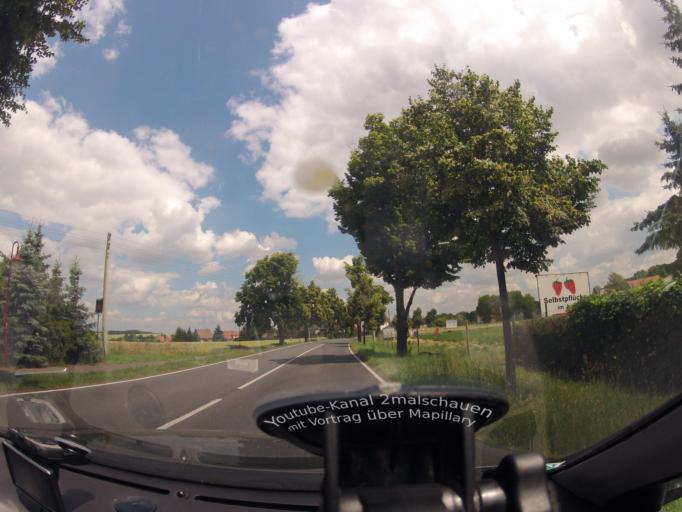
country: DE
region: Saxony
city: Jesewitz
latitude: 51.4217
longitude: 12.5576
